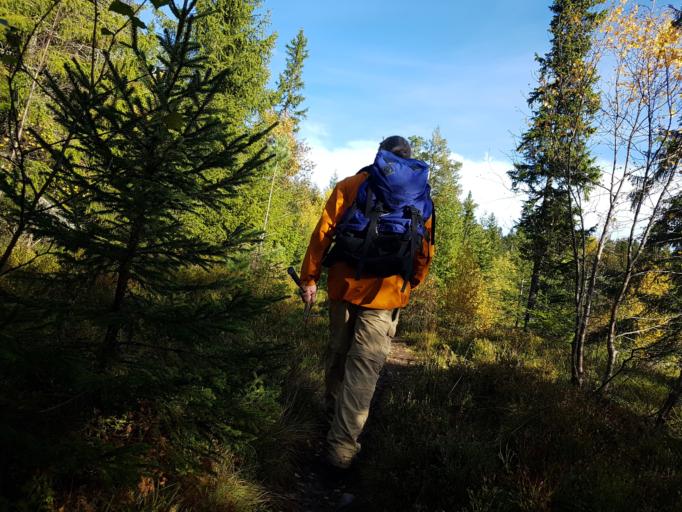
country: NO
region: Sor-Trondelag
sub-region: Trondheim
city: Trondheim
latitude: 63.4239
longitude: 10.2906
